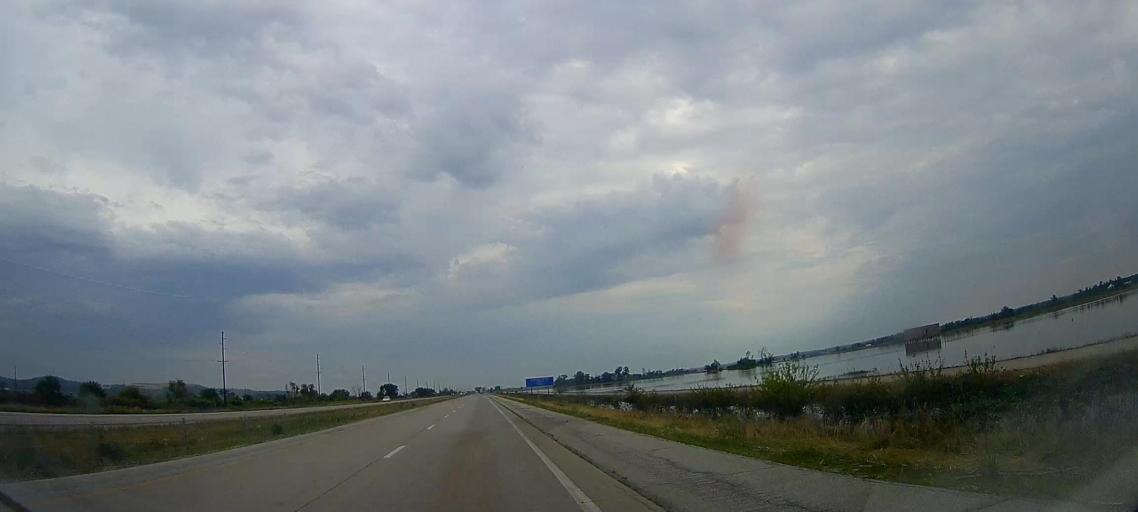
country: US
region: Iowa
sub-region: Pottawattamie County
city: Carter Lake
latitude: 41.3804
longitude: -95.8997
